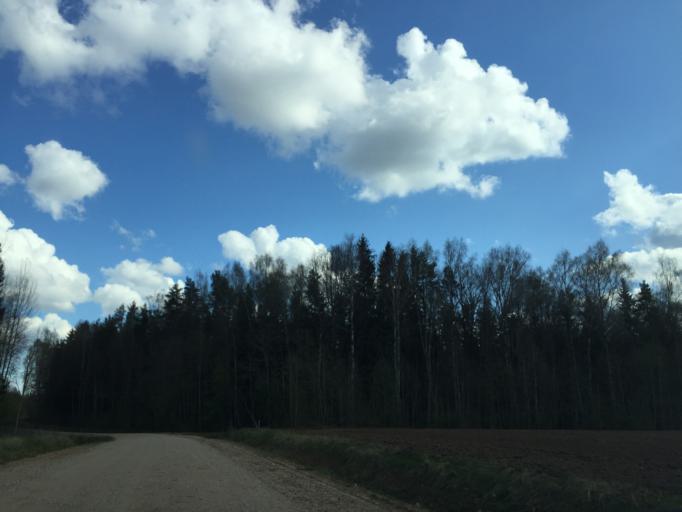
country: LV
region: Beverina
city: Murmuiza
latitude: 57.4540
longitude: 25.5318
